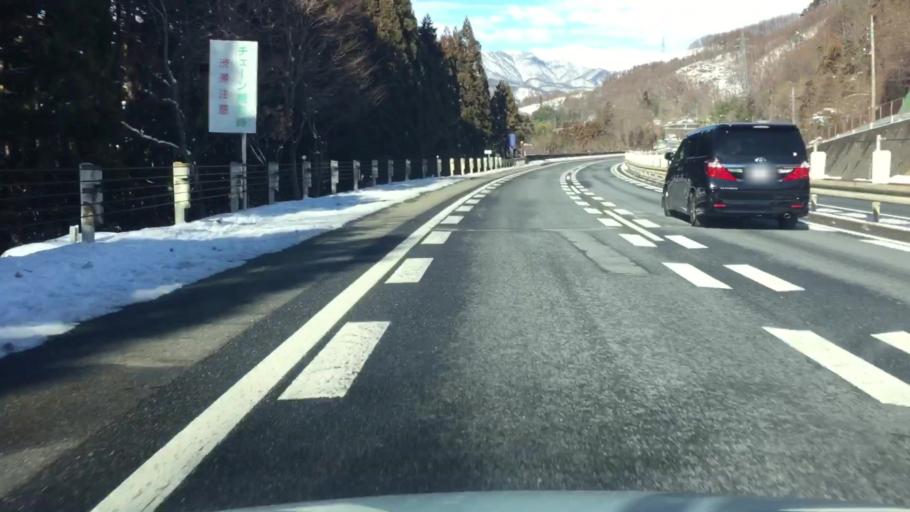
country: JP
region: Gunma
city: Numata
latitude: 36.6931
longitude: 138.9935
